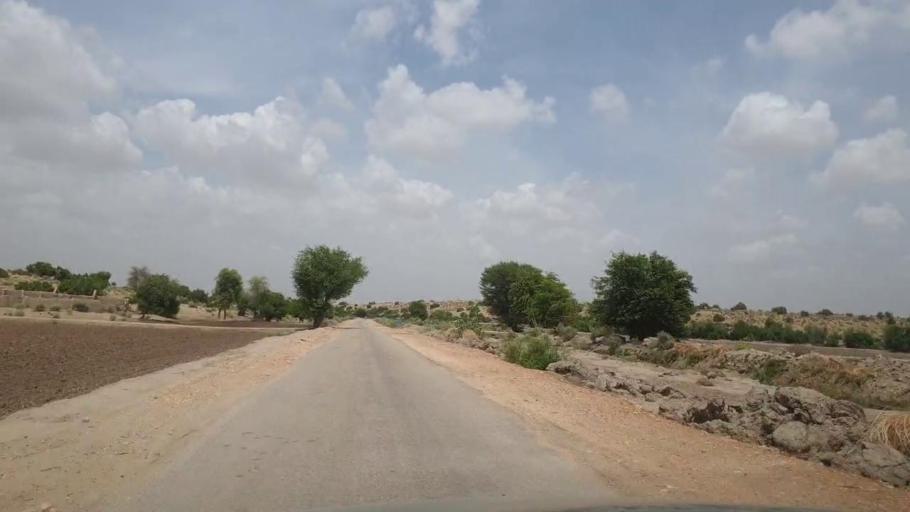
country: PK
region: Sindh
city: Kot Diji
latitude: 27.2092
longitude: 69.0944
